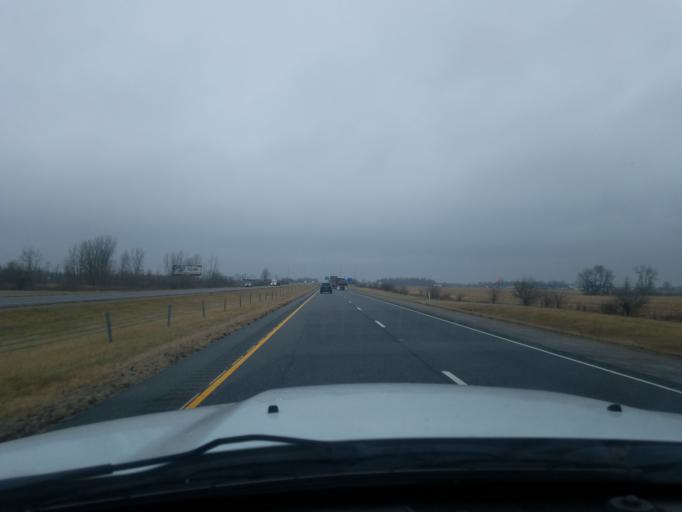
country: US
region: Indiana
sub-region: Delaware County
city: Yorktown
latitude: 40.2667
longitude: -85.5578
